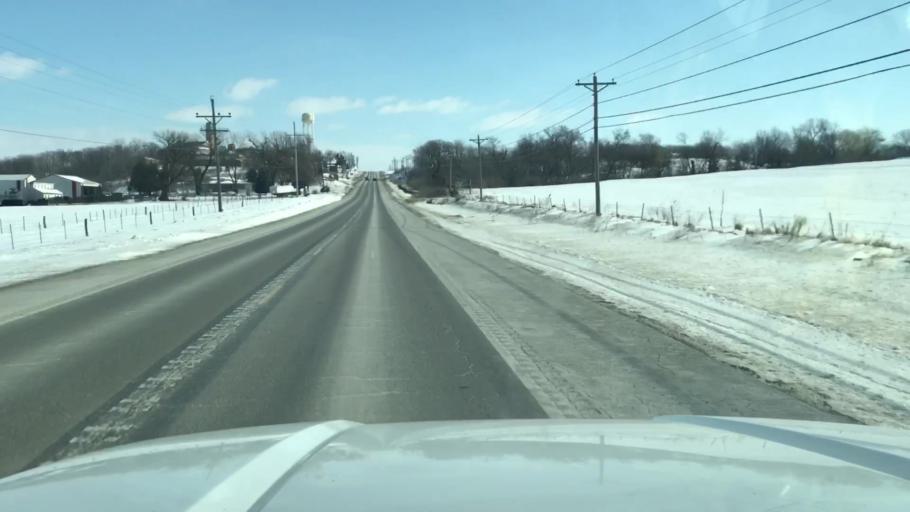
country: US
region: Missouri
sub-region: Nodaway County
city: Maryville
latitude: 40.3449
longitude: -94.8218
